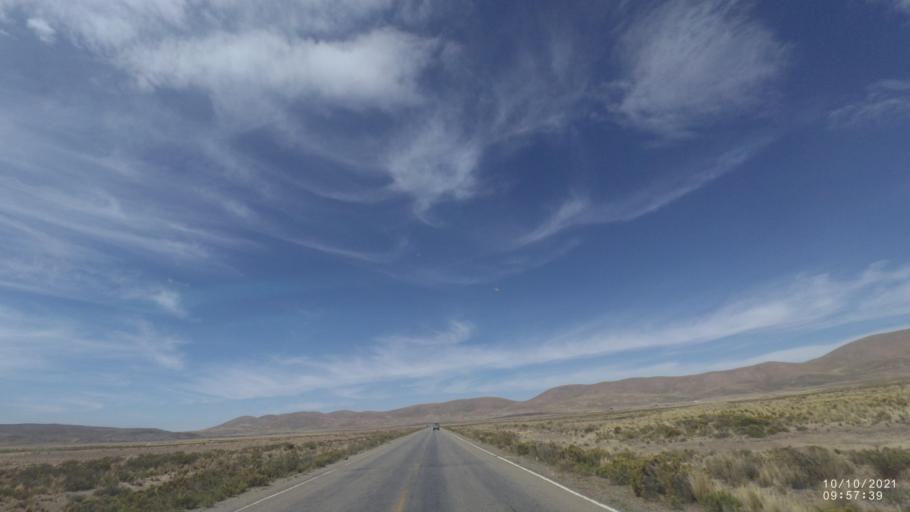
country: BO
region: La Paz
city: Colquiri
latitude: -17.3396
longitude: -67.3873
